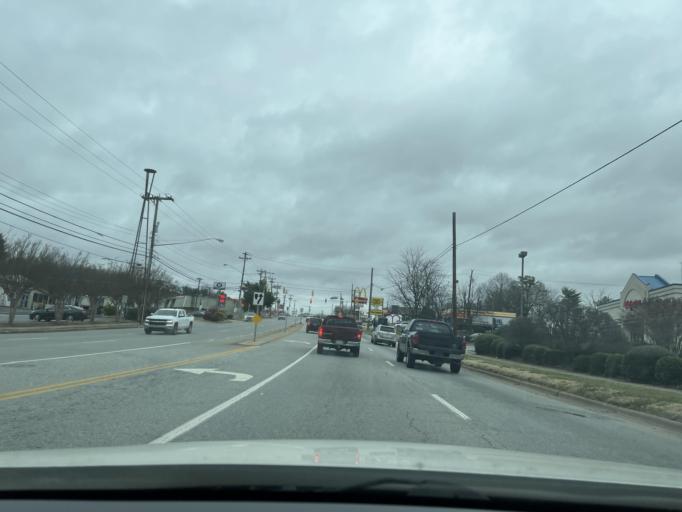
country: US
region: North Carolina
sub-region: Guilford County
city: Greensboro
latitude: 36.0384
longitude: -79.8001
